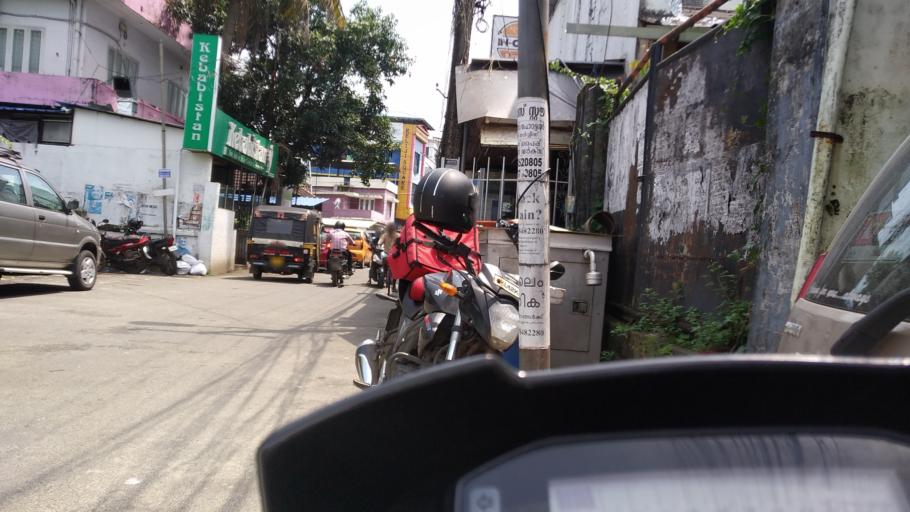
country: IN
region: Kerala
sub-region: Ernakulam
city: Cochin
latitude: 9.9559
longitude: 76.2928
